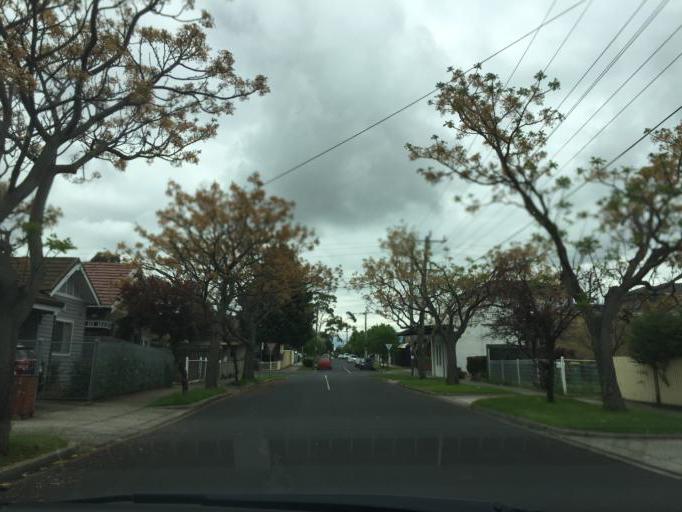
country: AU
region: Victoria
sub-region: Maribyrnong
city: West Footscray
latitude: -37.7937
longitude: 144.8731
